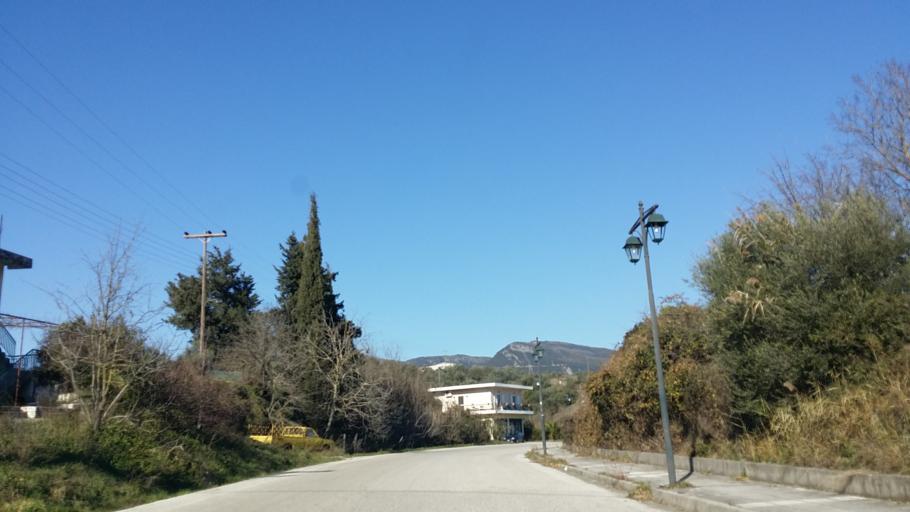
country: GR
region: West Greece
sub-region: Nomos Aitolias kai Akarnanias
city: Sardinia
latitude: 38.8551
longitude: 21.3362
